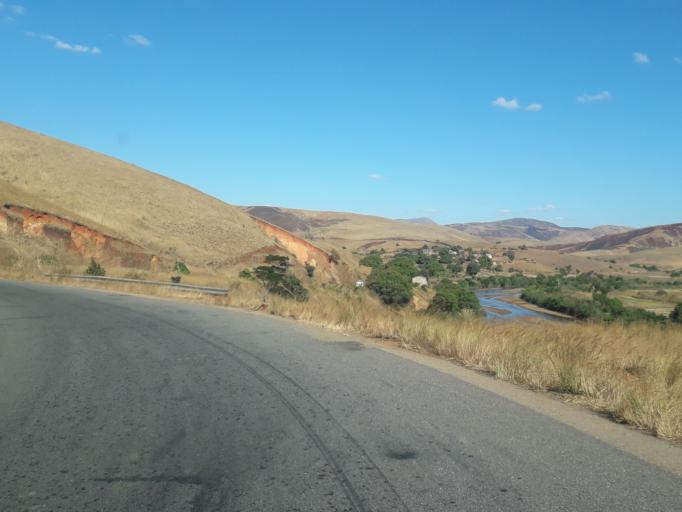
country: MG
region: Analamanga
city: Ankazobe
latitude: -17.6428
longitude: 46.9594
